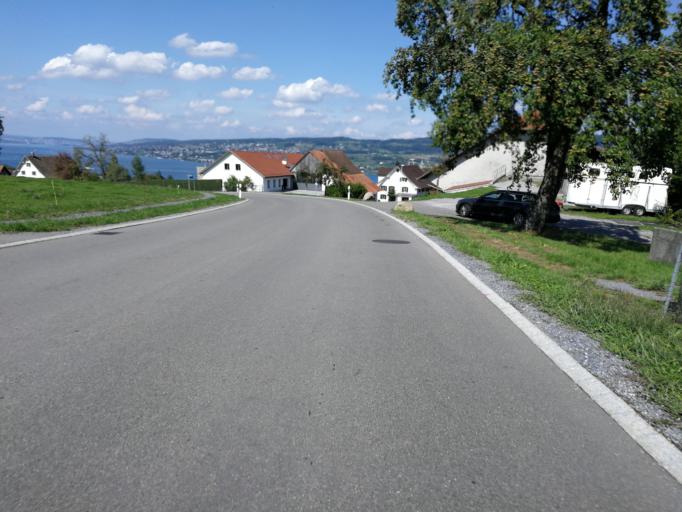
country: CH
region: Zurich
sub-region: Bezirk Horgen
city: Au / Unter-Dorf
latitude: 47.2388
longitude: 8.6276
